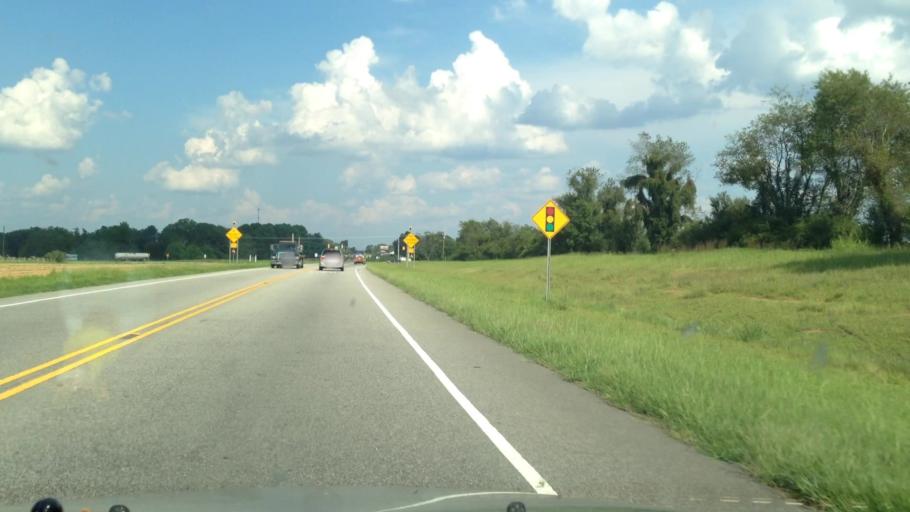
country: US
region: North Carolina
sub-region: Lee County
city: Broadway
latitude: 35.4388
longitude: -79.0401
